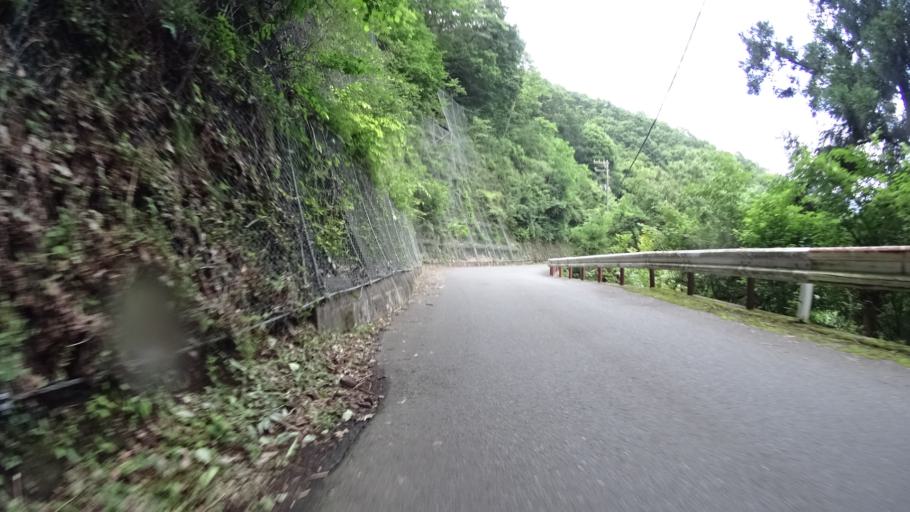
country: JP
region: Kanagawa
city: Hadano
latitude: 35.4977
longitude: 139.2226
